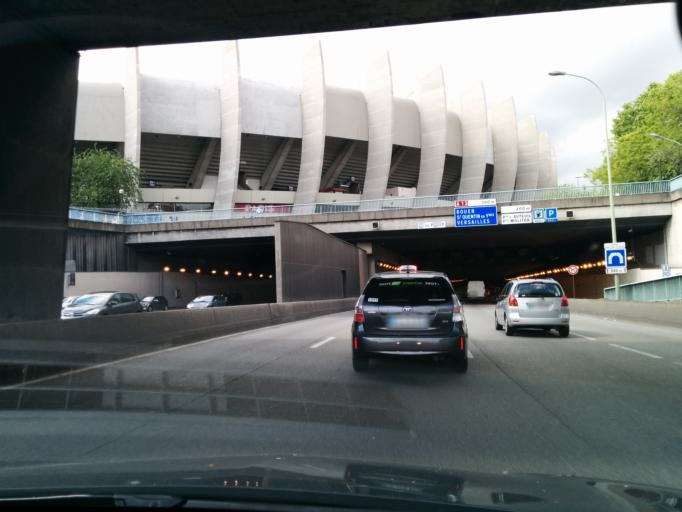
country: FR
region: Ile-de-France
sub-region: Departement des Hauts-de-Seine
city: Boulogne-Billancourt
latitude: 48.8402
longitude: 2.2541
